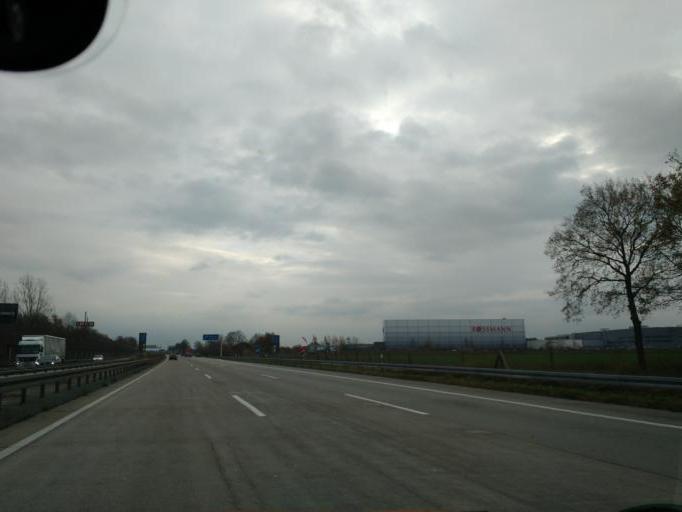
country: DE
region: Lower Saxony
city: Isernhagen Farster Bauerschaft
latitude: 52.4954
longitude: 9.8323
